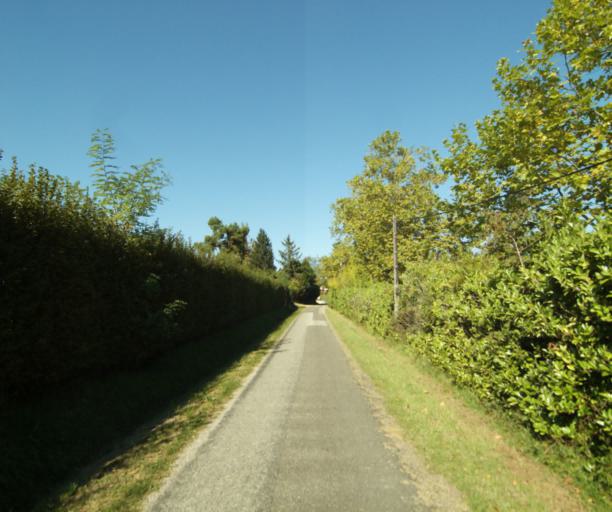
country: FR
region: Midi-Pyrenees
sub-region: Departement du Gers
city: Cazaubon
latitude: 43.9525
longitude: -0.0288
